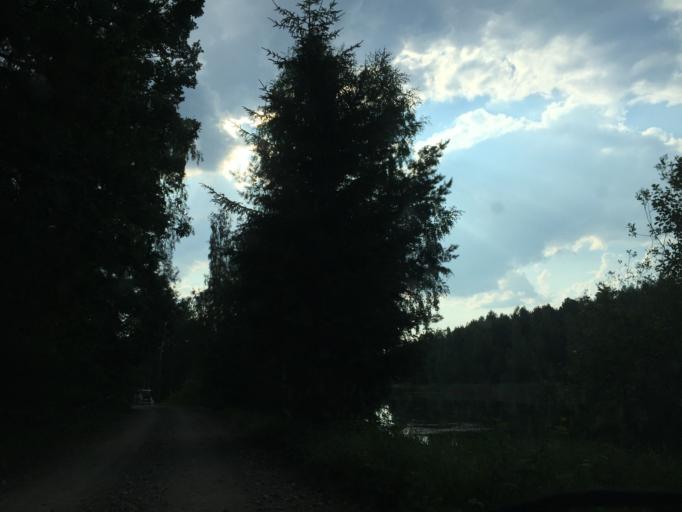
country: LT
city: Zagare
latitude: 56.4488
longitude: 23.1353
